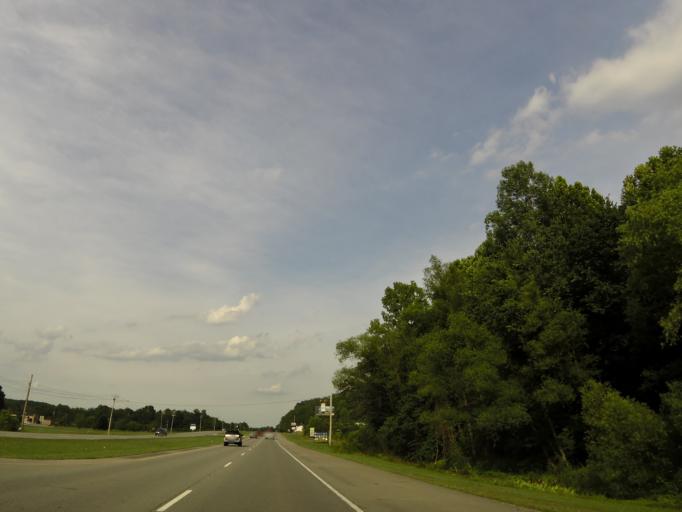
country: US
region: Tennessee
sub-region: Humphreys County
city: Waverly
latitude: 36.0763
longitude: -87.8564
